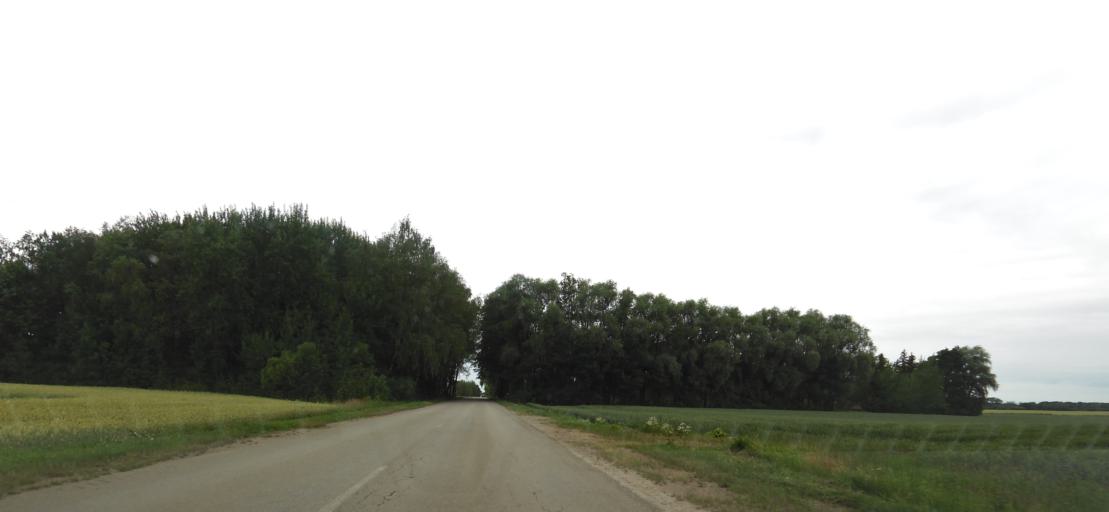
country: LT
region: Panevezys
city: Pasvalys
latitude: 56.0867
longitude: 24.5020
